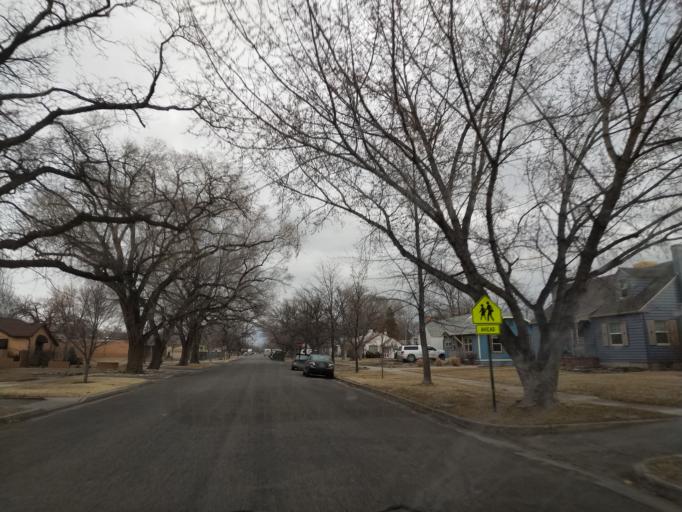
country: US
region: Colorado
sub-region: Mesa County
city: Grand Junction
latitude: 39.0723
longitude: -108.5501
